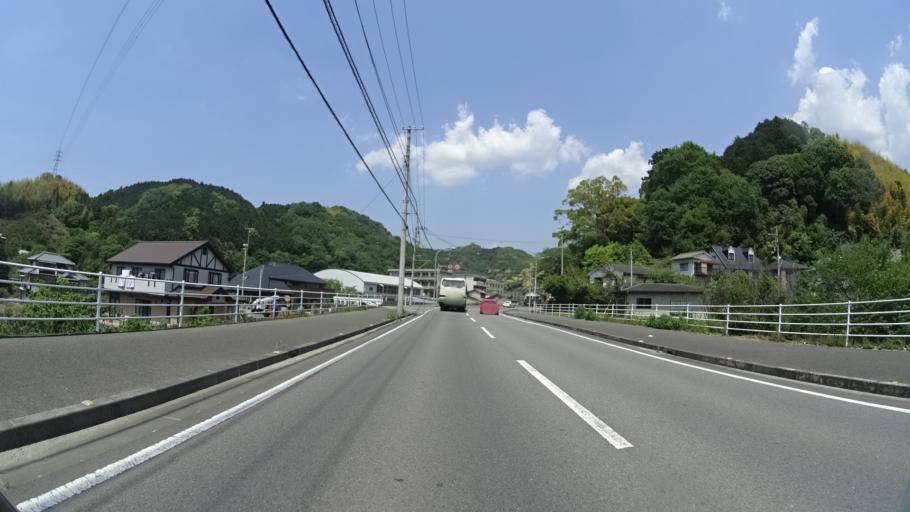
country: JP
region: Ehime
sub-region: Shikoku-chuo Shi
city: Matsuyama
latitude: 33.8588
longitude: 132.8132
